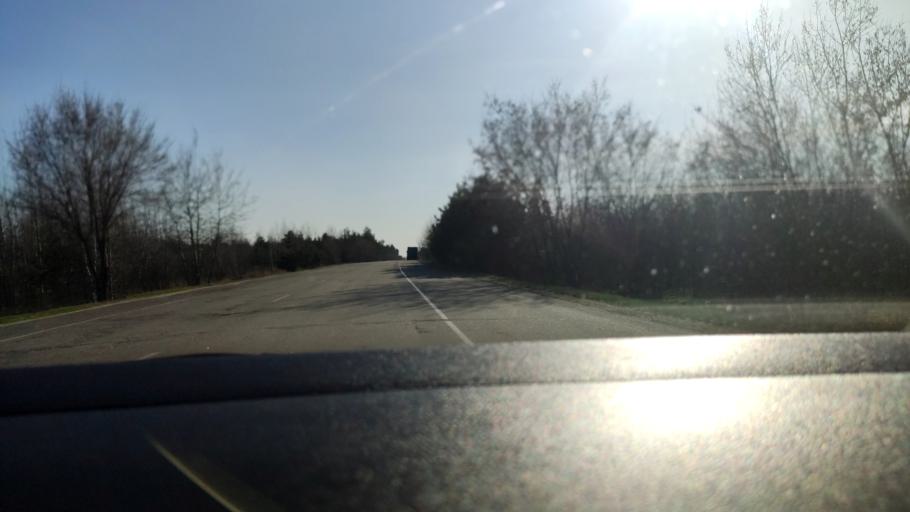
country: RU
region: Voronezj
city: Kolodeznyy
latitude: 51.3710
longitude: 39.2058
